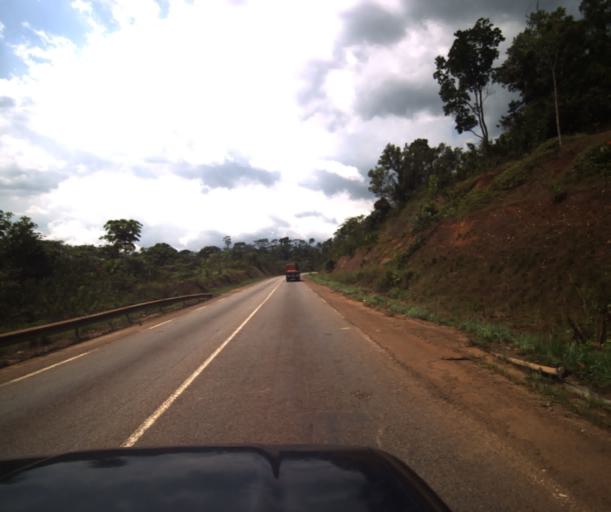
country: CM
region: Littoral
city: Edea
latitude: 3.8833
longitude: 10.0685
